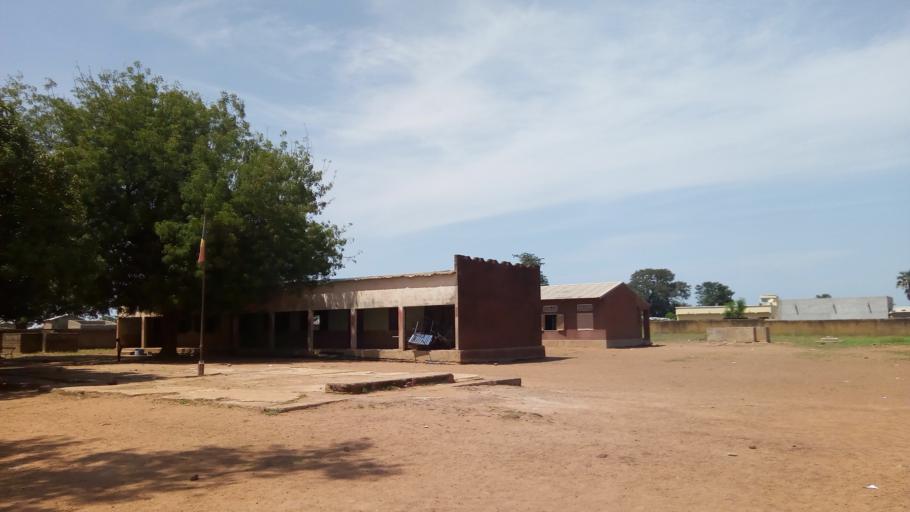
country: ML
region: Koulikoro
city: Kangaba
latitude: 11.7171
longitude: -8.6738
